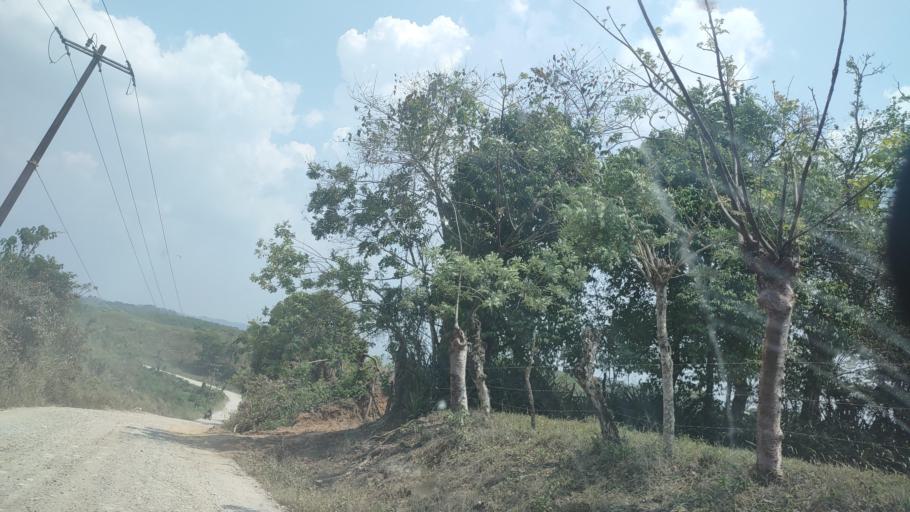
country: MX
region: Tabasco
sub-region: Huimanguillo
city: Francisco Rueda
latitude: 17.6095
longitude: -93.9115
